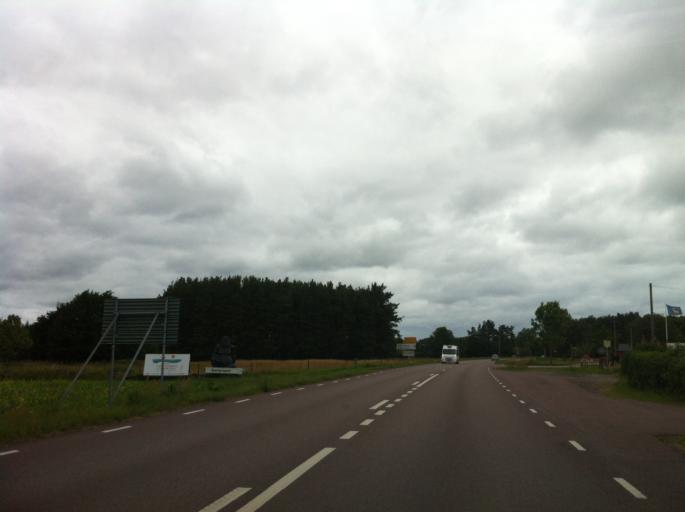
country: SE
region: Kalmar
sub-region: Borgholms Kommun
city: Borgholm
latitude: 57.1877
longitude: 17.0301
